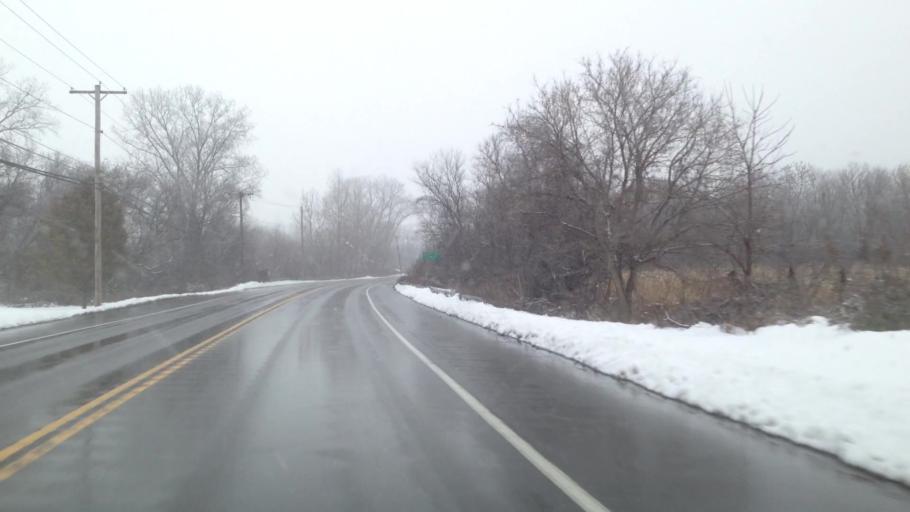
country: US
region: New York
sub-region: Onondaga County
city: Elbridge
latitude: 43.0385
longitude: -76.4122
